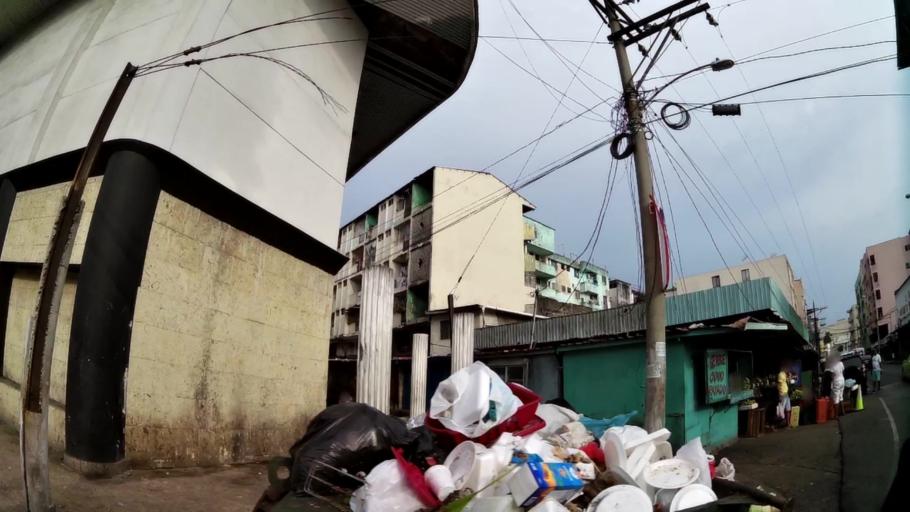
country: PA
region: Panama
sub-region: Distrito de Panama
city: Ancon
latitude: 8.9633
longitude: -79.5399
